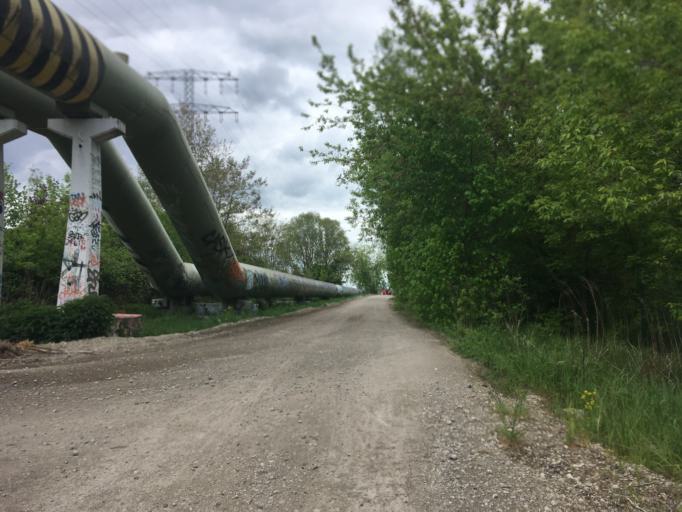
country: DE
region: Berlin
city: Falkenberg
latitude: 52.5510
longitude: 13.5299
